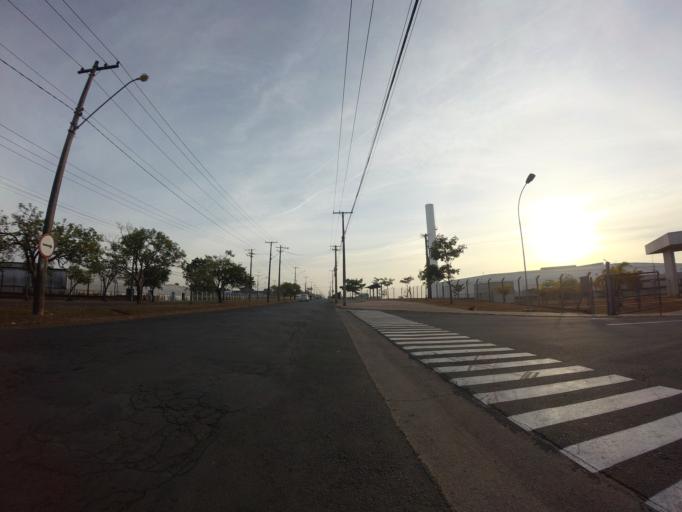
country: BR
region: Sao Paulo
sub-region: Piracicaba
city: Piracicaba
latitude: -22.7351
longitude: -47.5888
